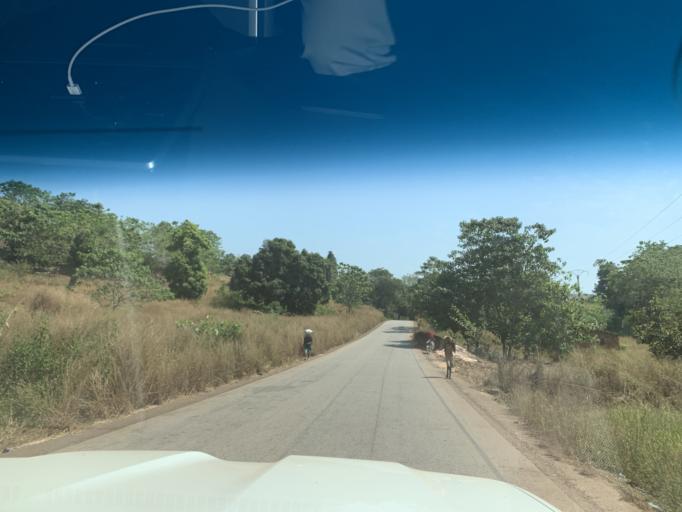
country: GN
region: Kindia
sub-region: Kindia
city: Kindia
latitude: 10.0963
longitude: -12.6218
